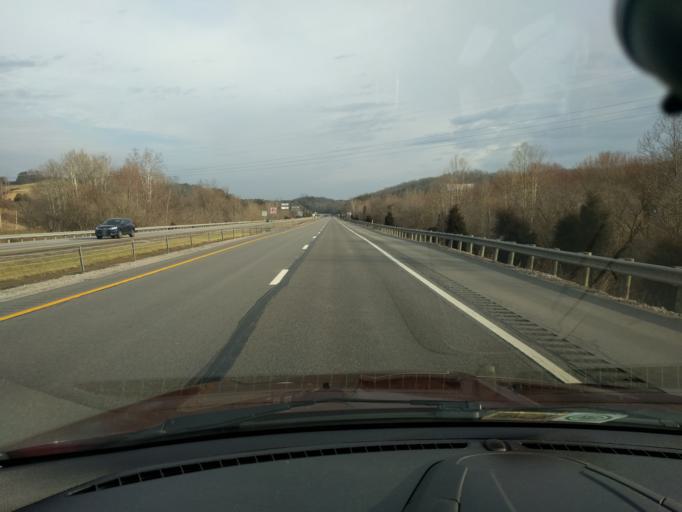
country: US
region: West Virginia
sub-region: Jackson County
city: Ripley
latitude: 38.8253
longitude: -81.7263
